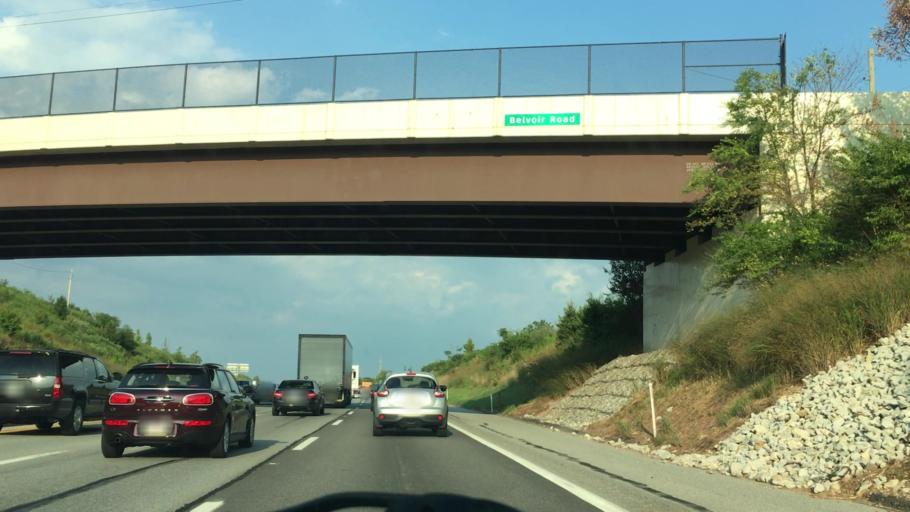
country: US
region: Pennsylvania
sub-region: Montgomery County
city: Conshohocken
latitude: 40.1060
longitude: -75.3126
